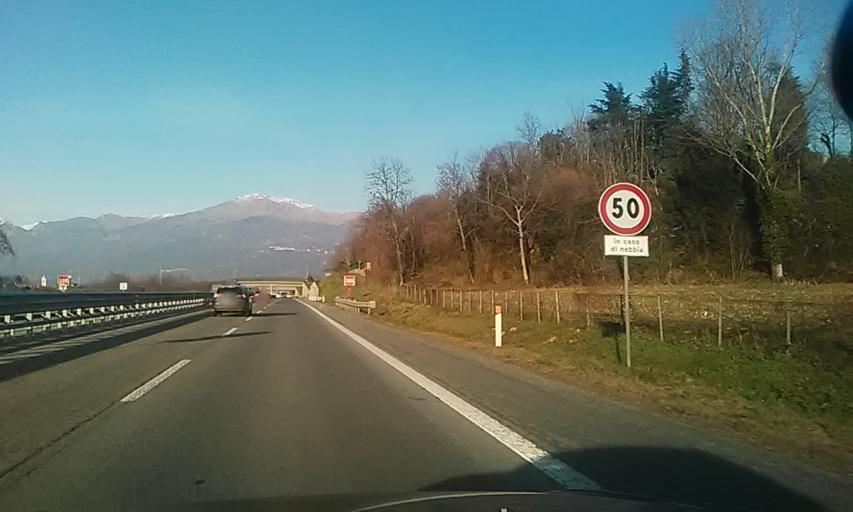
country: IT
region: Piedmont
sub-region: Provincia di Torino
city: Banchette
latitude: 45.4495
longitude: 7.8513
